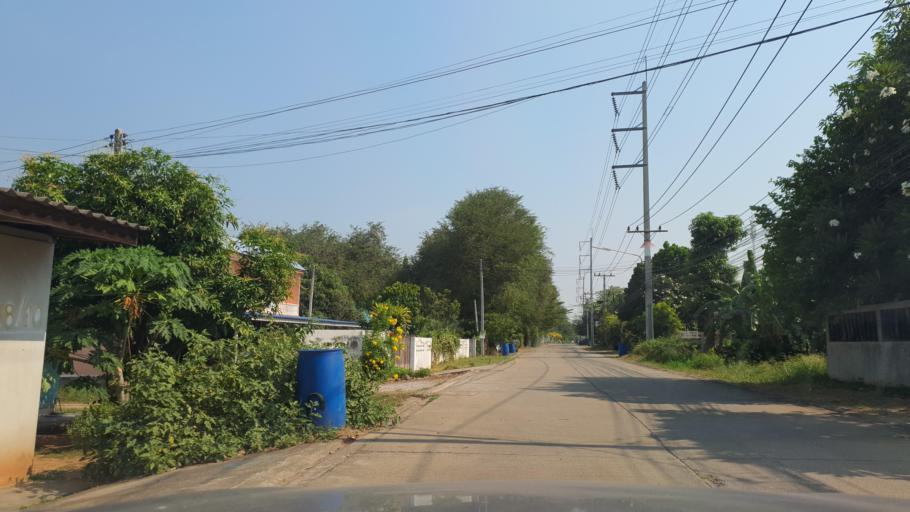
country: TH
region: Kanchanaburi
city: Kanchanaburi
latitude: 14.0624
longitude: 99.4854
